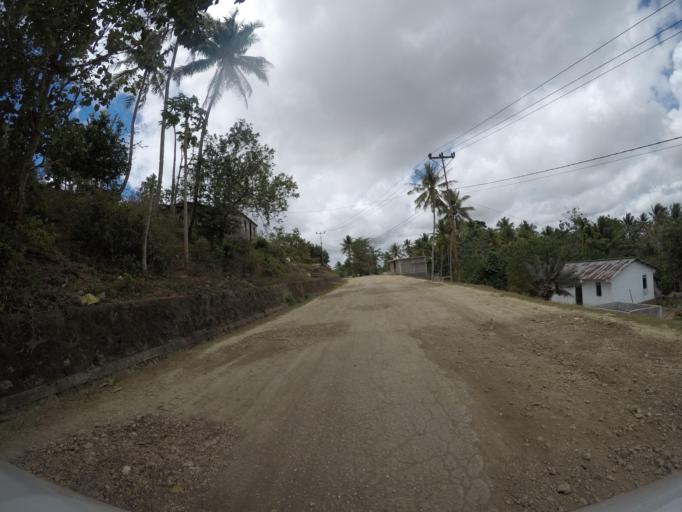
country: TL
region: Lautem
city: Lospalos
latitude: -8.4411
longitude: 126.9674
